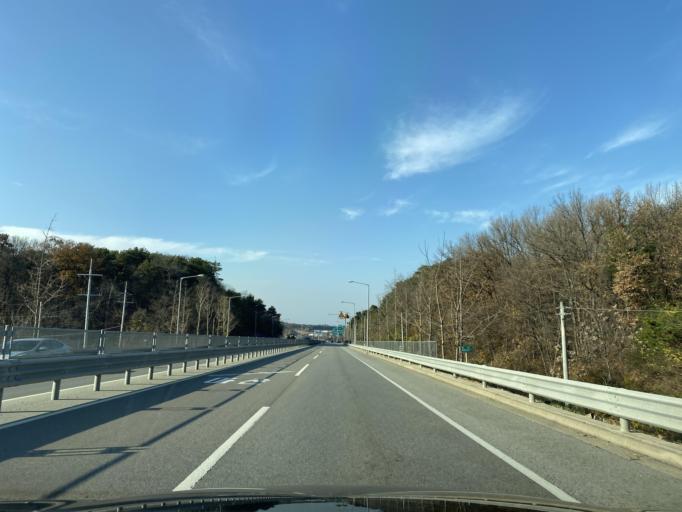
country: KR
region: Chungcheongnam-do
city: Asan
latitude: 36.7749
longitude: 126.9428
